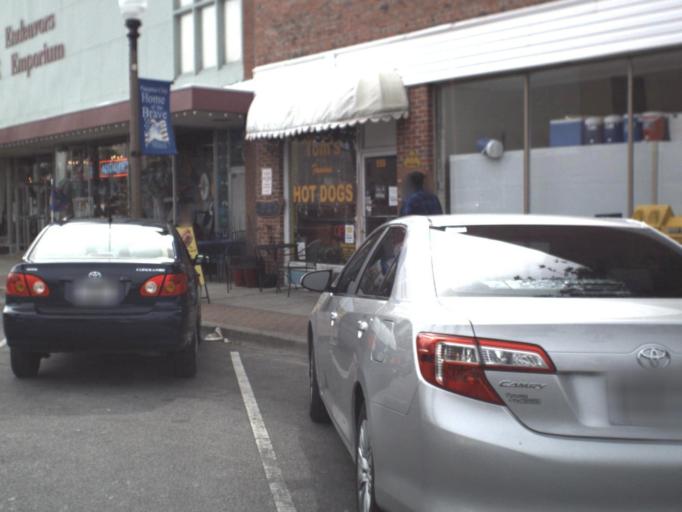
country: US
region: Florida
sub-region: Bay County
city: Panama City
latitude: 30.1582
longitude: -85.6604
